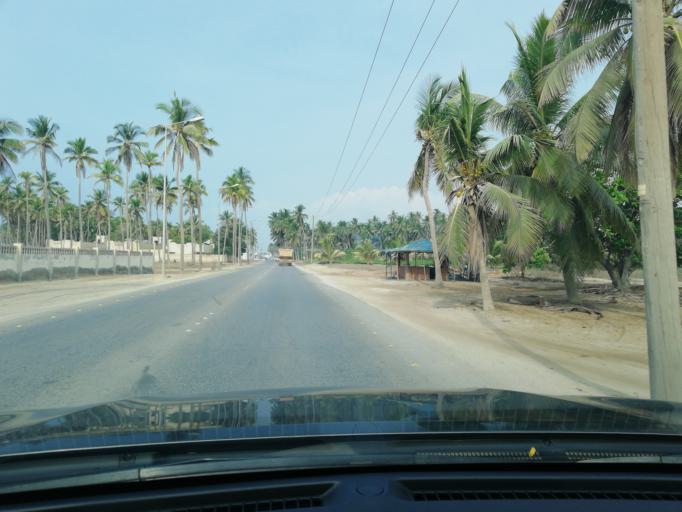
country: OM
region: Zufar
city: Salalah
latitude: 17.0045
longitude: 54.1200
